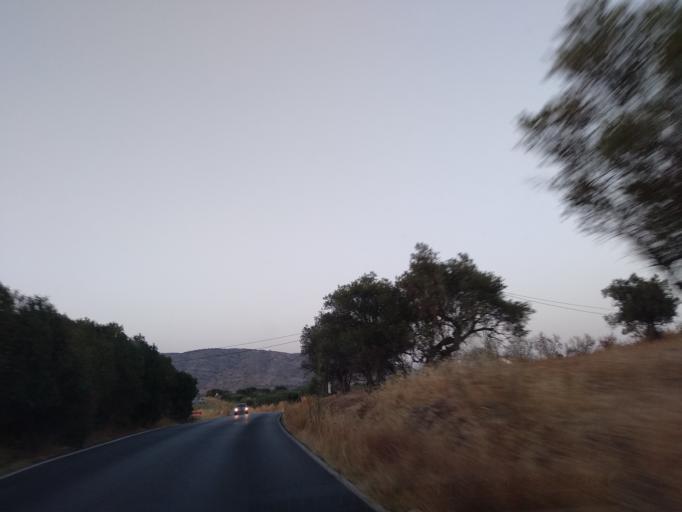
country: ES
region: Andalusia
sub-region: Provincia de Malaga
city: Cartama
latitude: 36.6777
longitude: -4.6591
